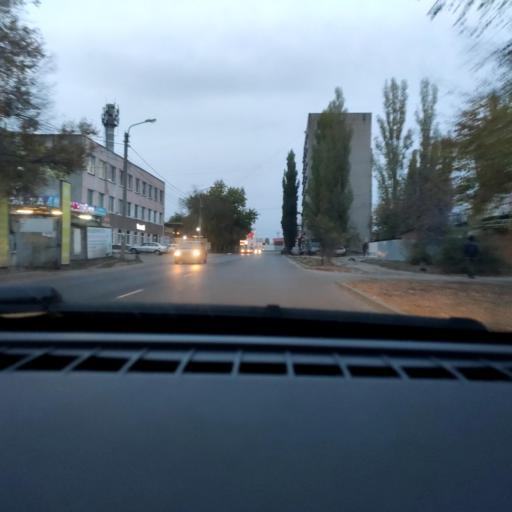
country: RU
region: Voronezj
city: Maslovka
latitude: 51.6333
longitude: 39.2729
